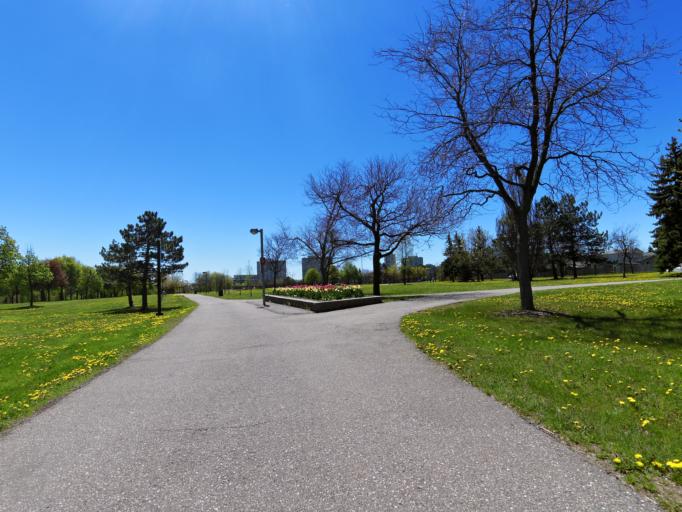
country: CA
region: Ontario
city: Brampton
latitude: 43.7260
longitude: -79.7272
